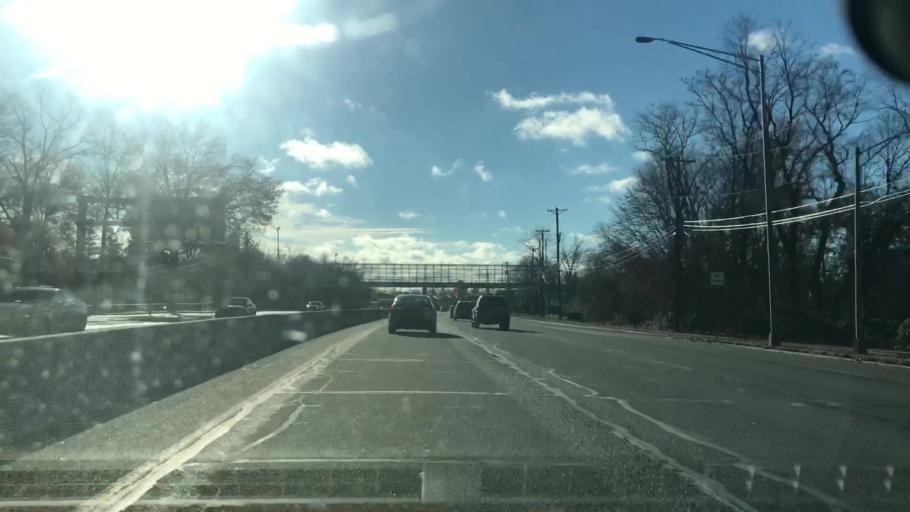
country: US
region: New Jersey
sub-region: Bergen County
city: Ho-Ho-Kus
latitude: 40.9928
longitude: -74.0962
